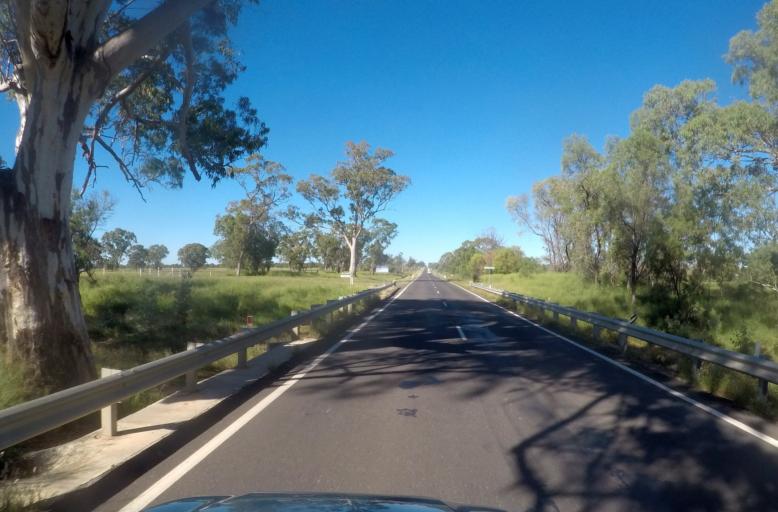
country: AU
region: Queensland
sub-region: Maranoa
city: Roma
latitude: -26.4844
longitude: 148.7964
